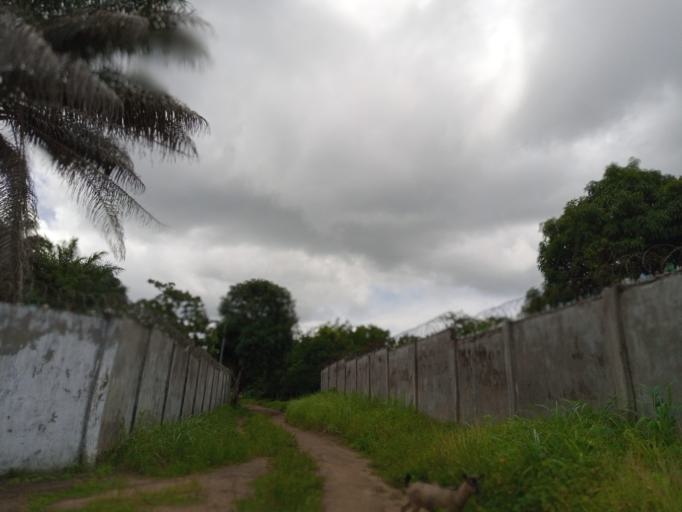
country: SL
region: Northern Province
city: Masoyila
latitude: 8.5886
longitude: -13.1687
